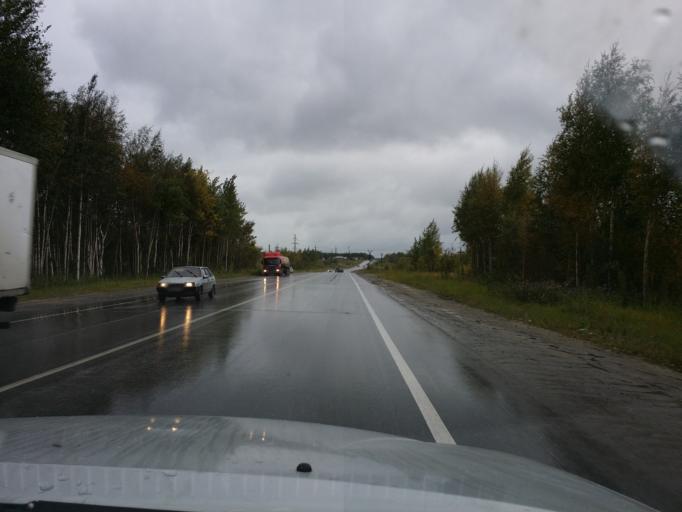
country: RU
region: Khanty-Mansiyskiy Avtonomnyy Okrug
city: Megion
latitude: 61.0632
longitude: 76.1151
